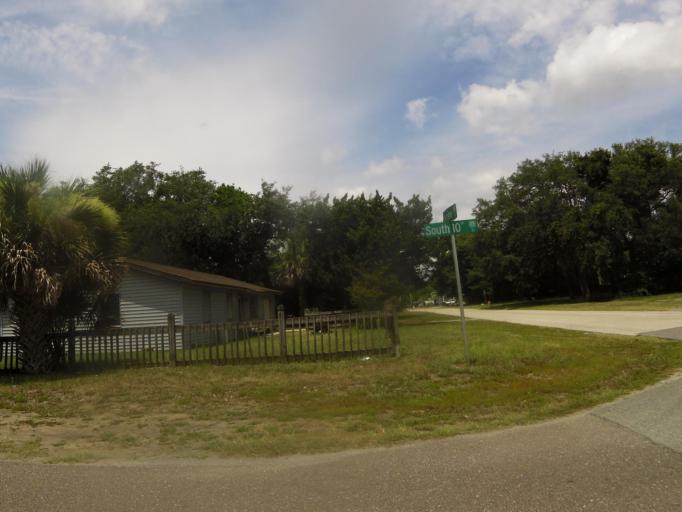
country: US
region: Florida
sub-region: Nassau County
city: Fernandina Beach
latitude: 30.6579
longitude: -81.4591
